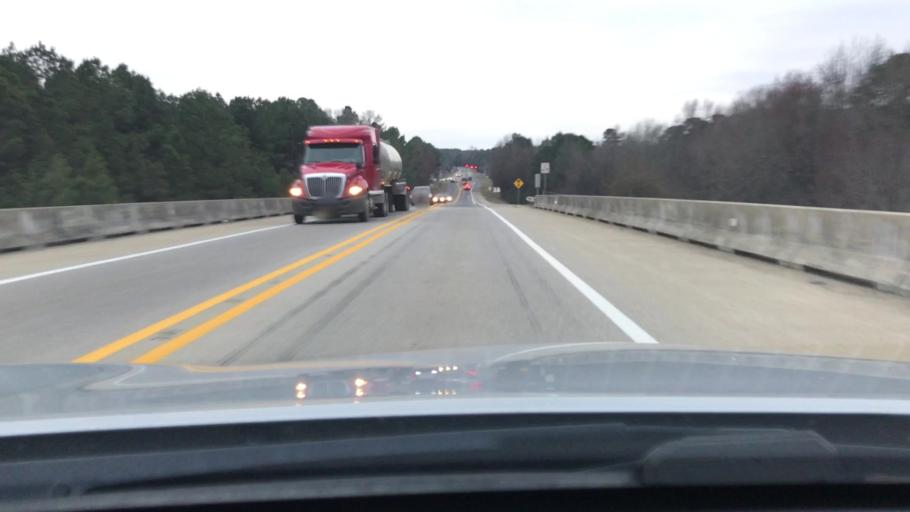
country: US
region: Arkansas
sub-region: Hempstead County
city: Hope
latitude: 33.6720
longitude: -93.5758
